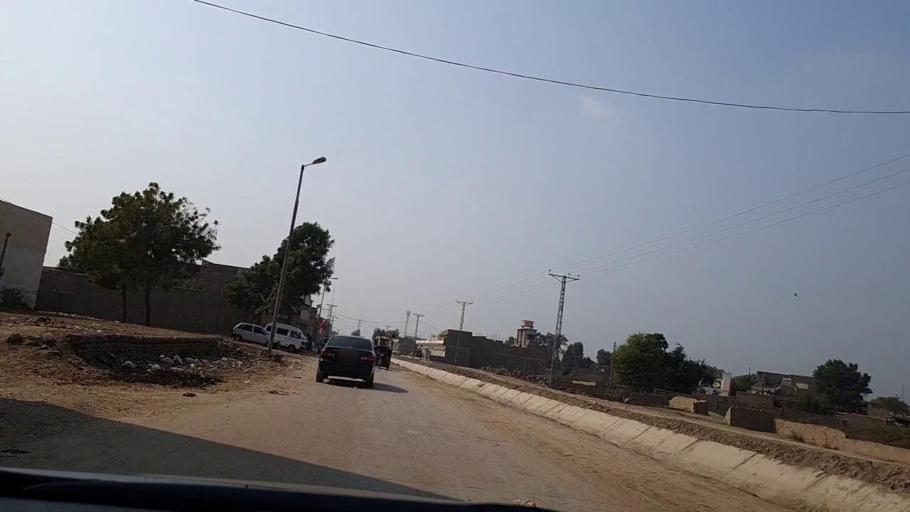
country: PK
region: Sindh
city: Sakrand
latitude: 26.1448
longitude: 68.2683
